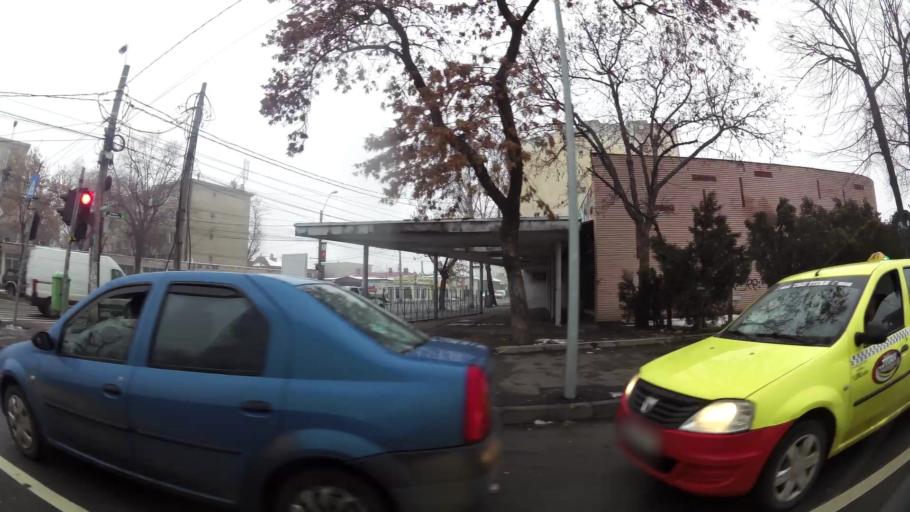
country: RO
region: Ilfov
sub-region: Comuna Chiajna
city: Rosu
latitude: 44.4638
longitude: 26.0412
